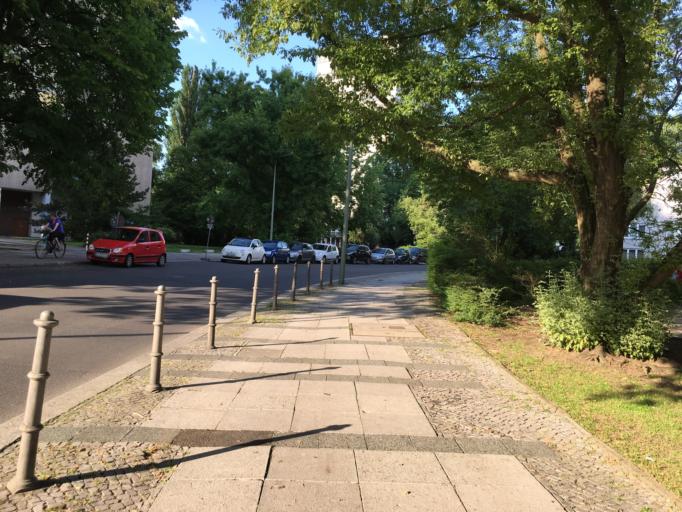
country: DE
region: Berlin
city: Hansaviertel
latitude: 52.5187
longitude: 13.3434
